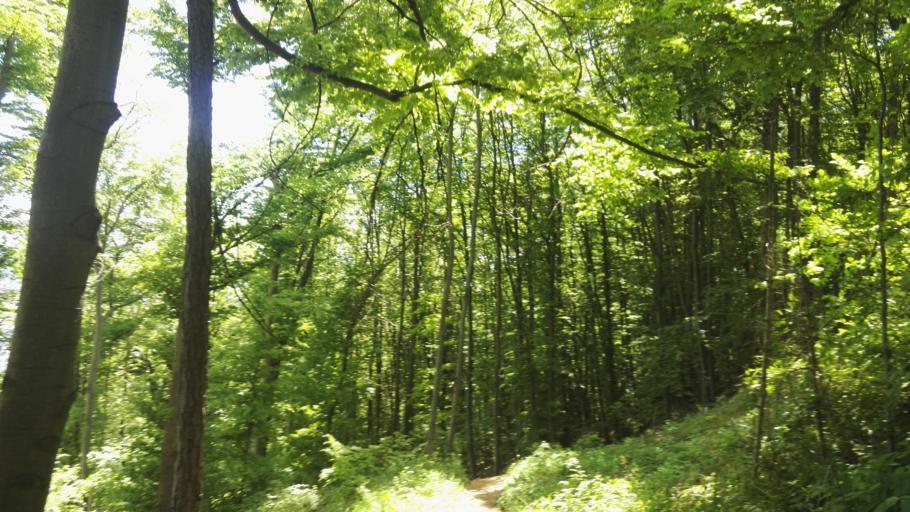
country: AT
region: Styria
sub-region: Graz Stadt
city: Goesting
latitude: 47.0888
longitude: 15.3885
